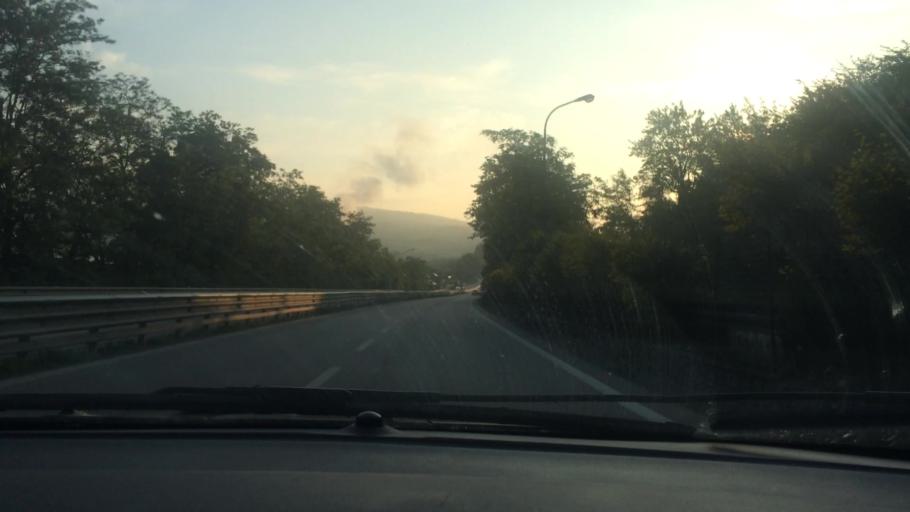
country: IT
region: Basilicate
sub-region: Provincia di Potenza
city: Potenza
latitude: 40.6332
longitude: 15.8242
